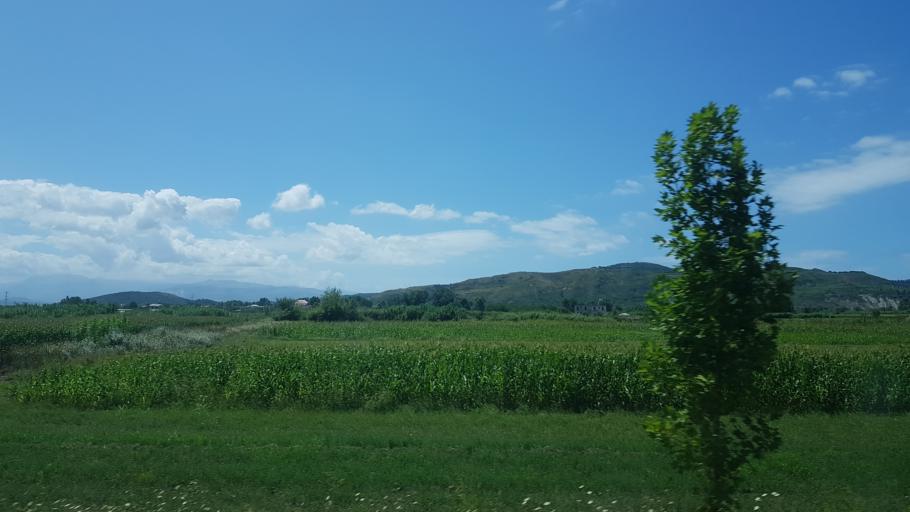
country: AL
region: Fier
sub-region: Rrethi i Fierit
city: Frakulla e Madhe
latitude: 40.6068
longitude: 19.5412
